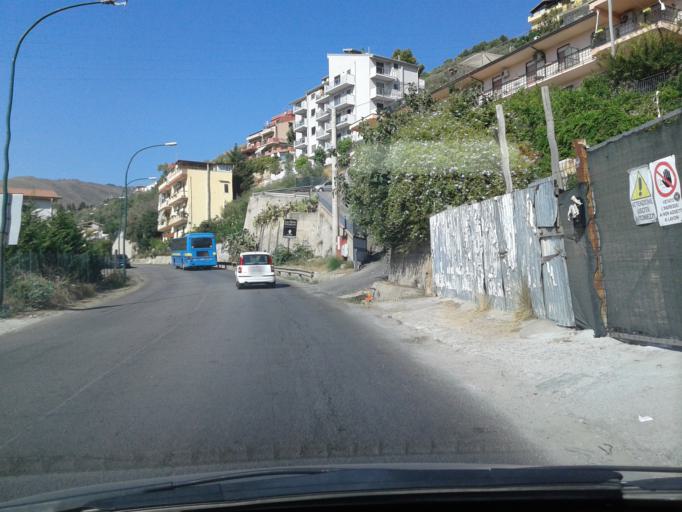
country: IT
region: Sicily
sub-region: Palermo
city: Monreale
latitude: 38.0758
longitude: 13.2800
